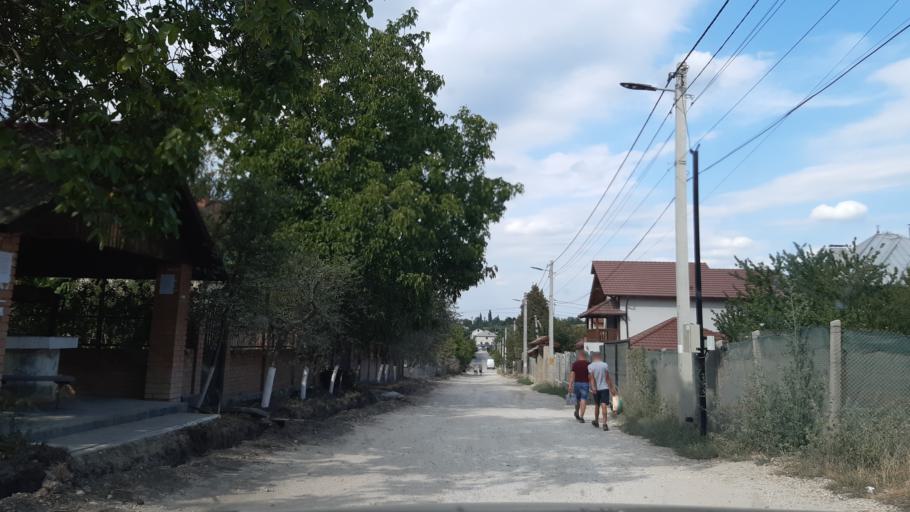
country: MD
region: Chisinau
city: Vatra
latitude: 47.0460
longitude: 28.7360
